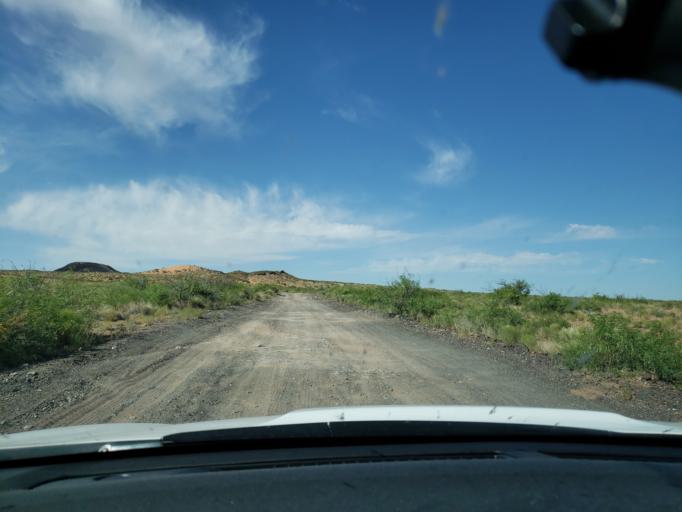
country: US
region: New Mexico
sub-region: Dona Ana County
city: San Miguel
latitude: 32.0833
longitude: -106.7898
